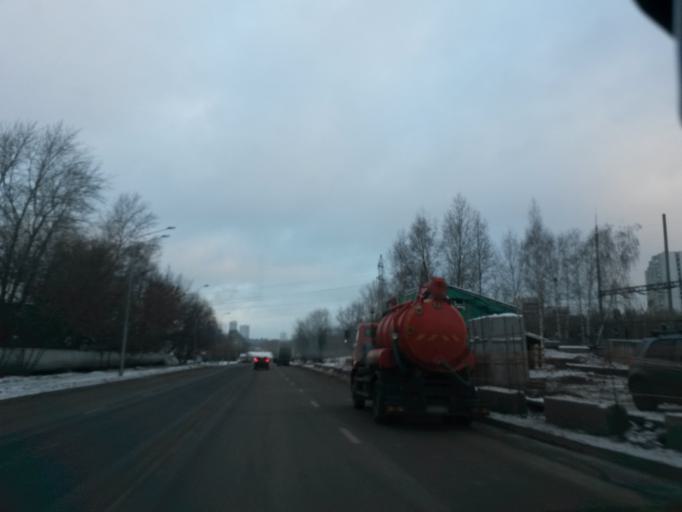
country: RU
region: Moscow
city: Amin'yevo
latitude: 55.6998
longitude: 37.4519
